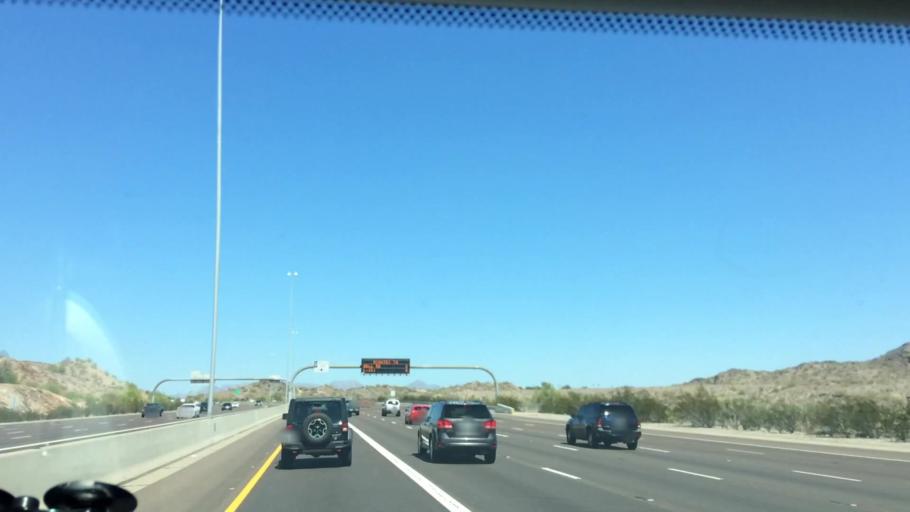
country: US
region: Arizona
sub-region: Maricopa County
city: Paradise Valley
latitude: 33.5646
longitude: -112.0328
